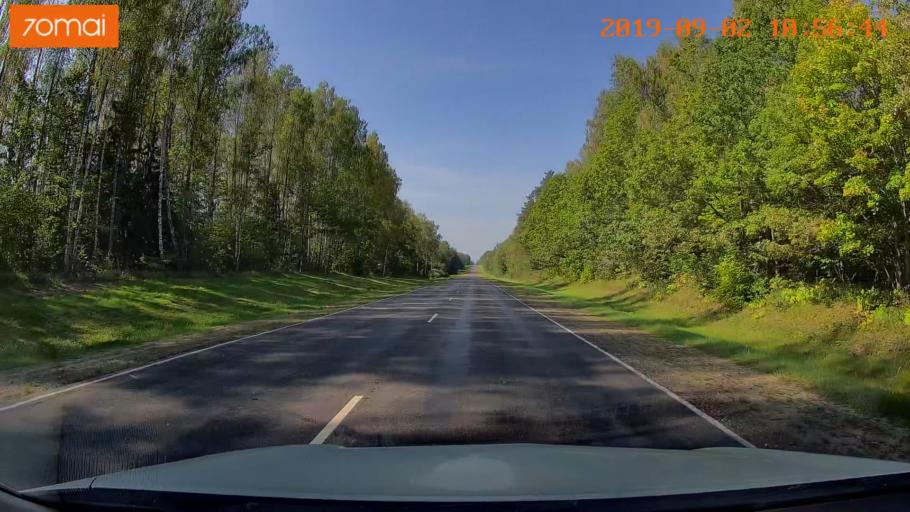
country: RU
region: Smolensk
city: Yekimovichi
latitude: 54.1764
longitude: 33.5011
